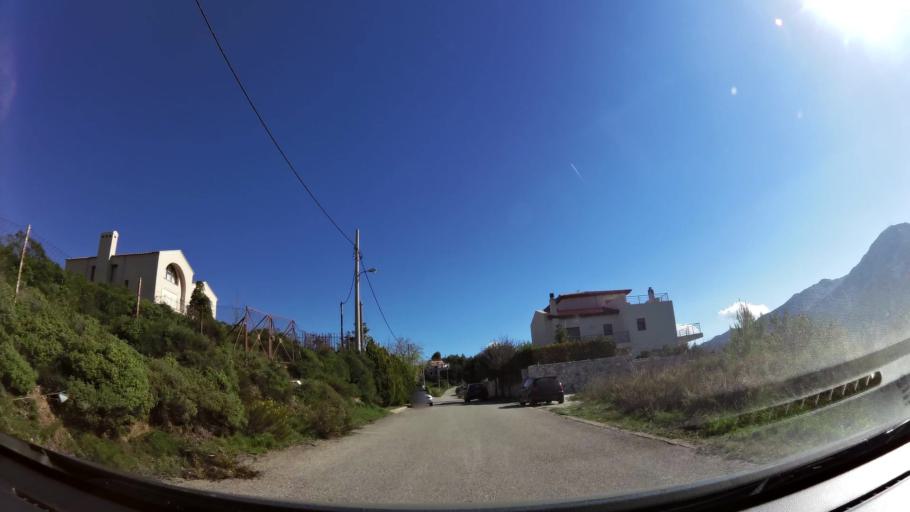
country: GR
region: Attica
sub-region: Nomarchia Anatolikis Attikis
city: Rodopoli
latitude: 38.1098
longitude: 23.8862
